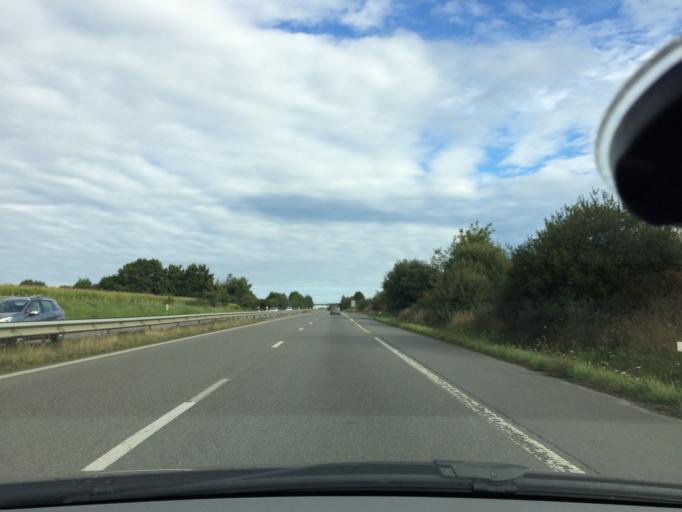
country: FR
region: Brittany
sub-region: Departement d'Ille-et-Vilaine
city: La Meziere
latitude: 48.2373
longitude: -1.7587
